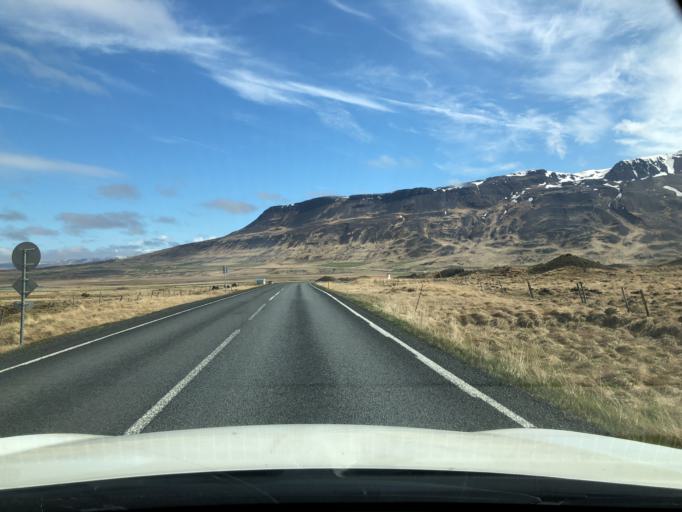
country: IS
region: Northwest
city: Saudarkrokur
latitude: 65.5031
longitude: -20.3910
